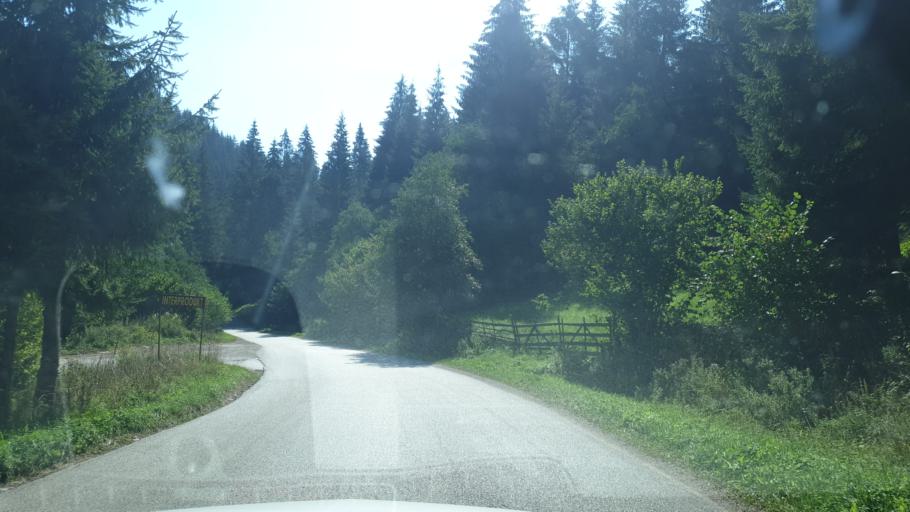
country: RS
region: Central Serbia
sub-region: Zlatiborski Okrug
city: Nova Varos
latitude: 43.4565
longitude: 19.8391
